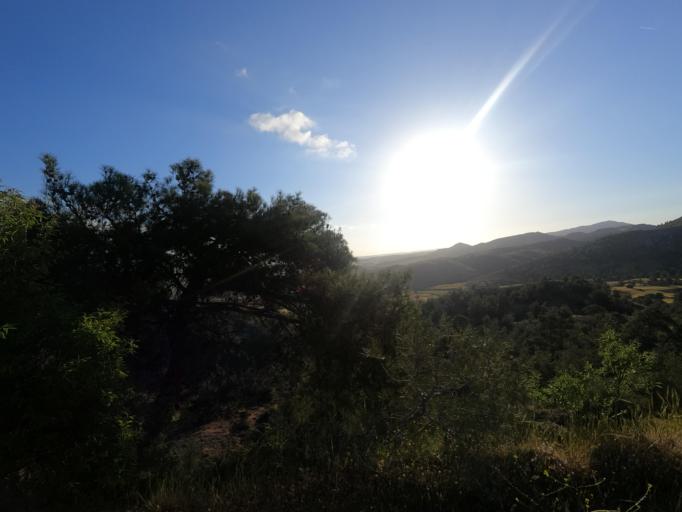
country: CY
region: Lefkosia
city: Astromeritis
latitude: 35.0676
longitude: 33.0379
